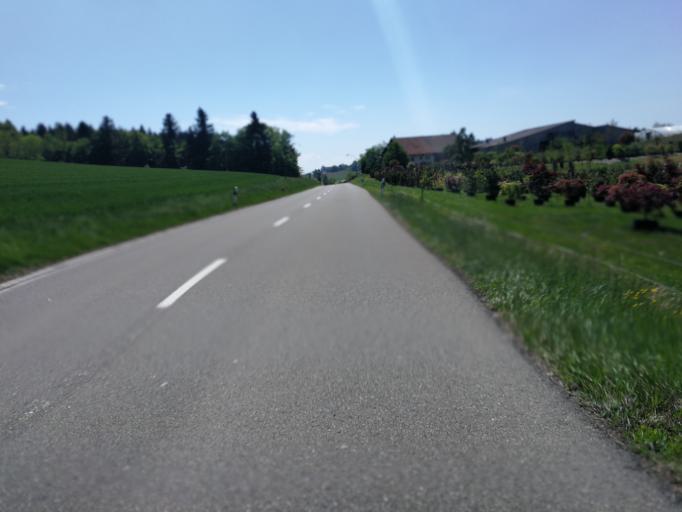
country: CH
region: Zurich
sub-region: Bezirk Uster
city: Aesch
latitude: 47.3137
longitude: 8.6409
